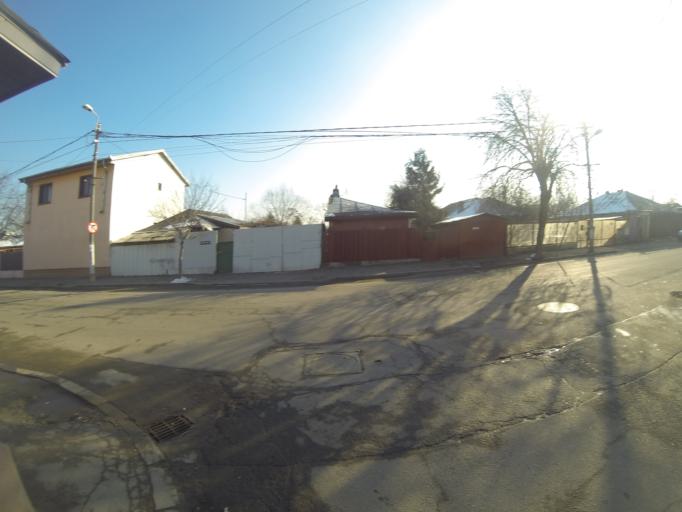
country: RO
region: Bucuresti
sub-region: Municipiul Bucuresti
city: Bucuresti
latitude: 44.3916
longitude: 26.0635
